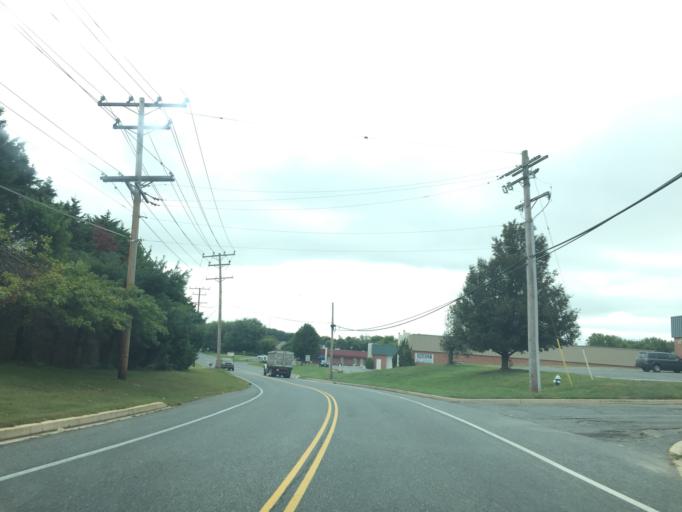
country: US
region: Maryland
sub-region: Harford County
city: Bel Air North
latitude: 39.5793
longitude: -76.3707
